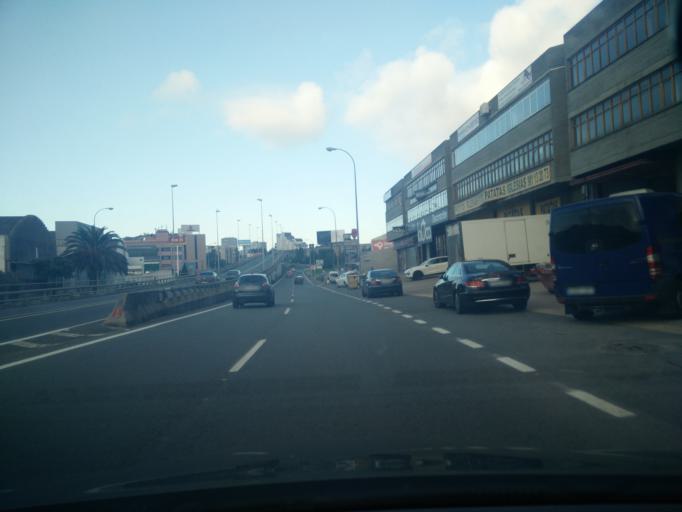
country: ES
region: Galicia
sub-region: Provincia da Coruna
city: A Coruna
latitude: 43.3477
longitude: -8.4238
